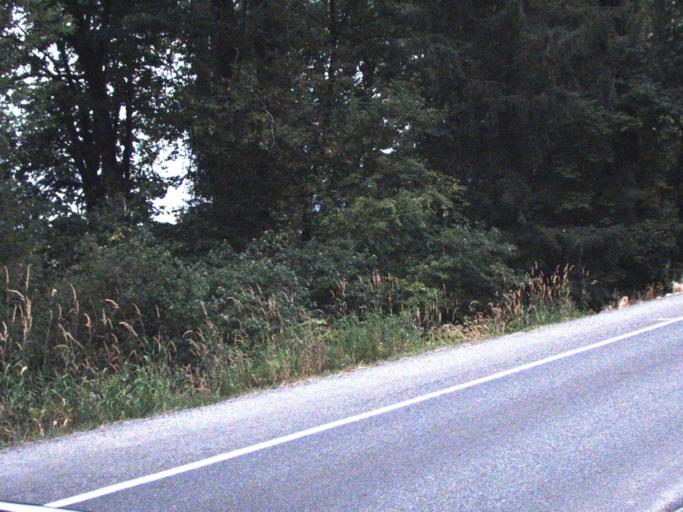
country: US
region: Washington
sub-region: Snohomish County
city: Monroe
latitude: 47.8051
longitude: -121.9806
